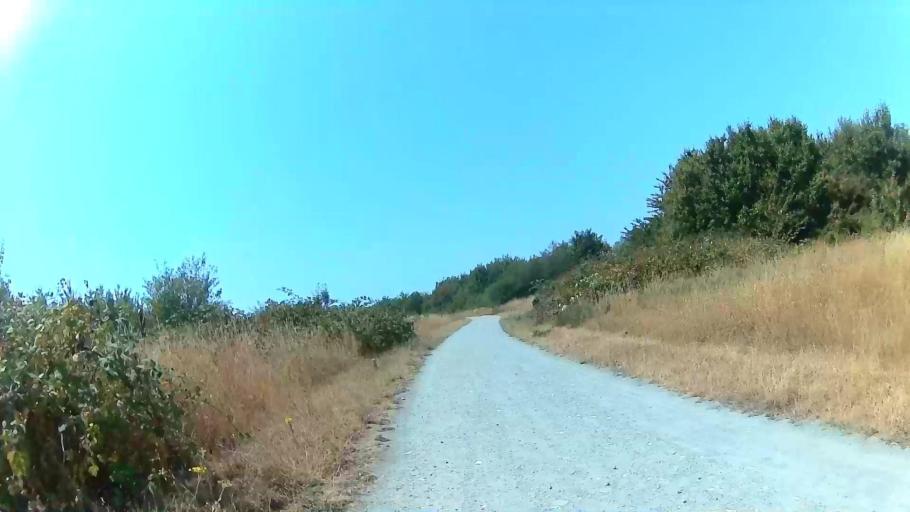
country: GB
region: England
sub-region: Greater London
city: Elm Park
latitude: 51.5319
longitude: 0.1956
